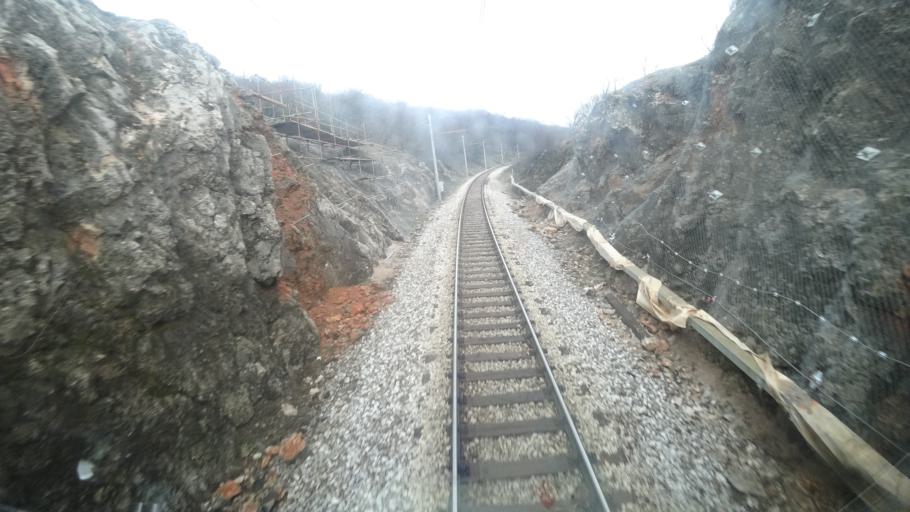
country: HR
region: Primorsko-Goranska
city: Hreljin
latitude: 45.2968
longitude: 14.6413
